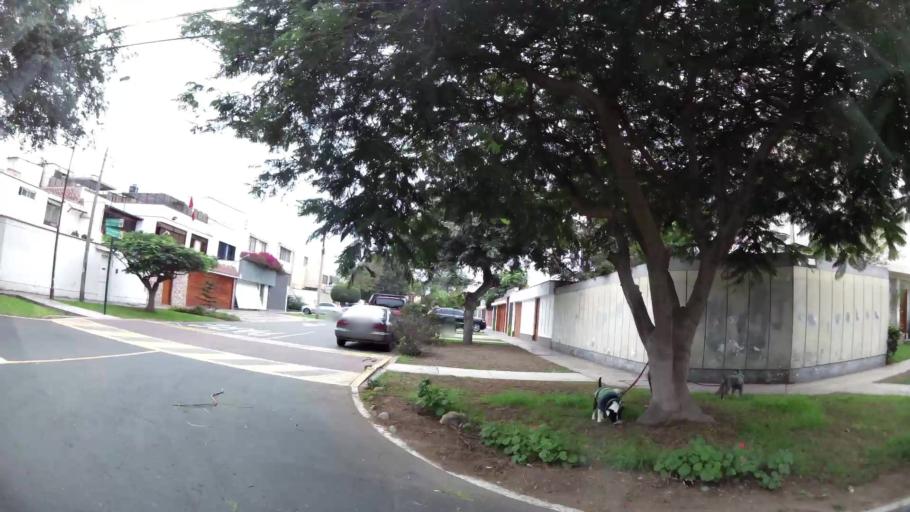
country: PE
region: Lima
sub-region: Lima
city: San Isidro
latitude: -12.0906
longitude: -77.0443
